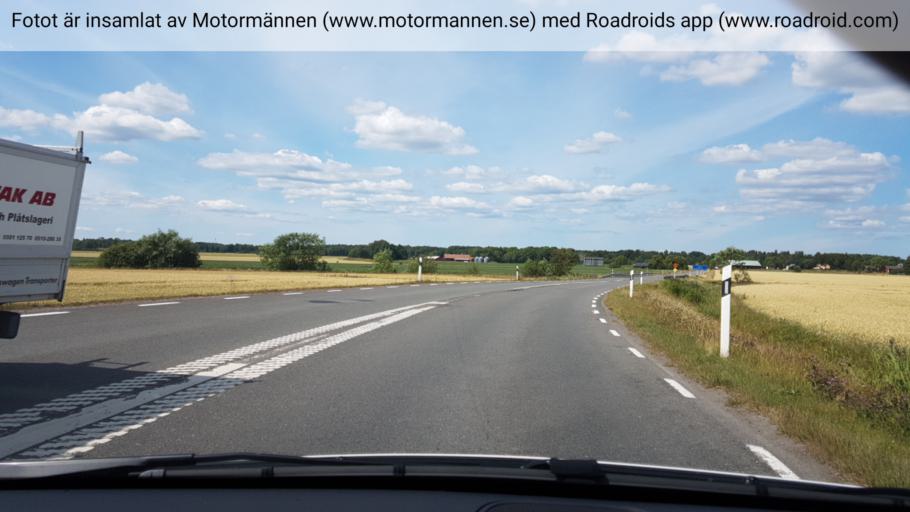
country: SE
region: Vaestra Goetaland
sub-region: Toreboda Kommun
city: Toereboda
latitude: 58.6092
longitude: 14.0085
